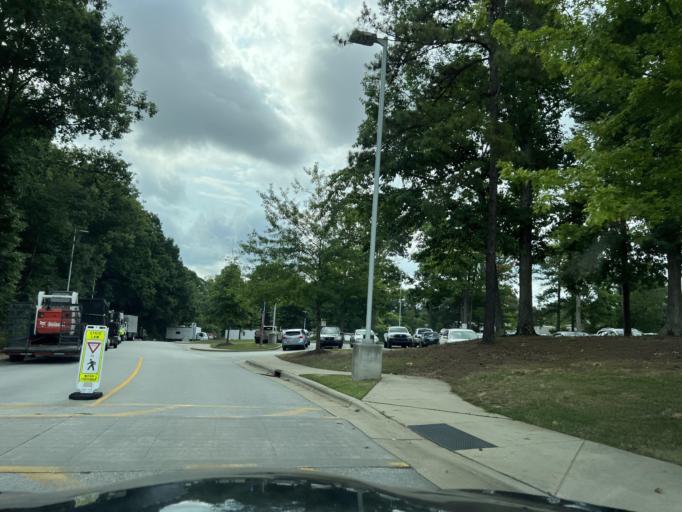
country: US
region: North Carolina
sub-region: Wake County
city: West Raleigh
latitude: 35.8202
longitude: -78.7022
